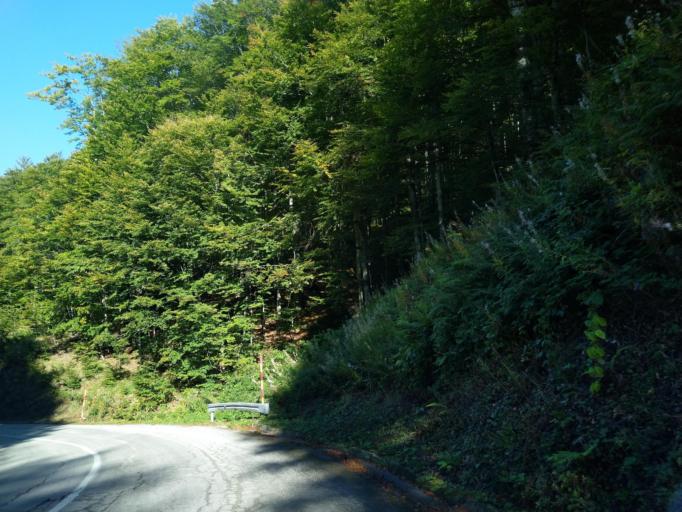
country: RS
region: Central Serbia
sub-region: Moravicki Okrug
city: Ivanjica
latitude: 43.4440
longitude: 20.2727
